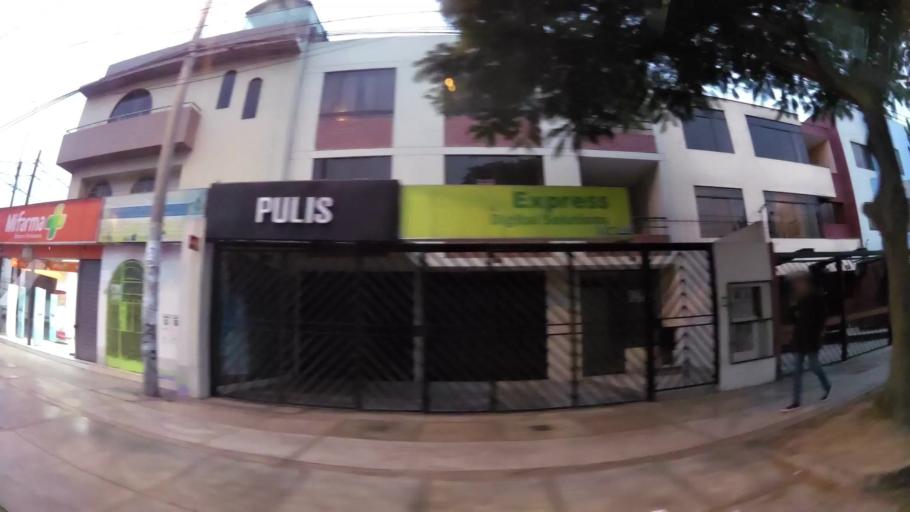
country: PE
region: Lima
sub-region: Lima
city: La Molina
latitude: -12.1016
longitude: -76.9493
